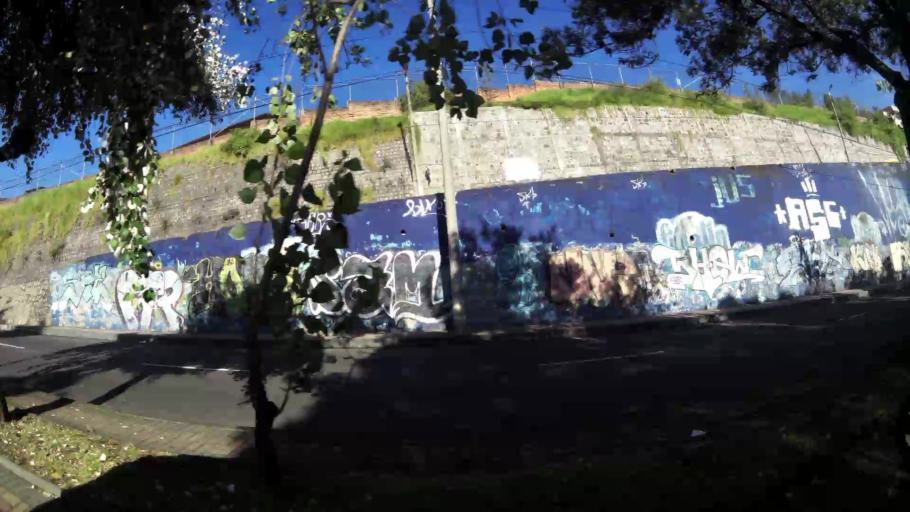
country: EC
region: Pichincha
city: Quito
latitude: -0.2393
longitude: -78.5187
